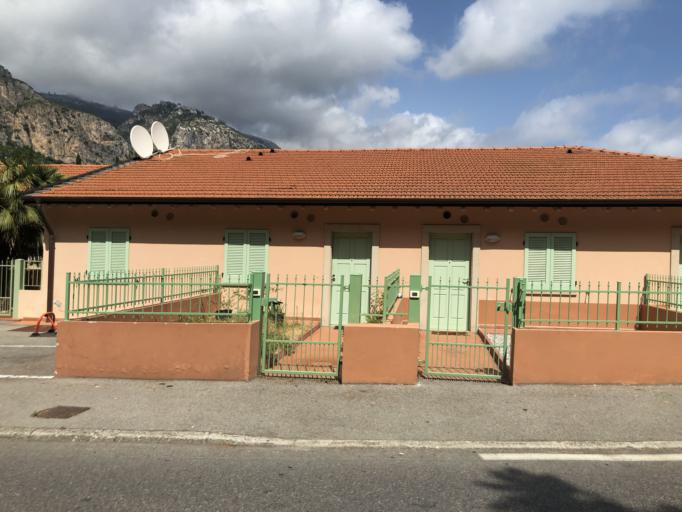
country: FR
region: Provence-Alpes-Cote d'Azur
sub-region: Departement des Alpes-Maritimes
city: Eze
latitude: 43.7171
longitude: 7.3495
